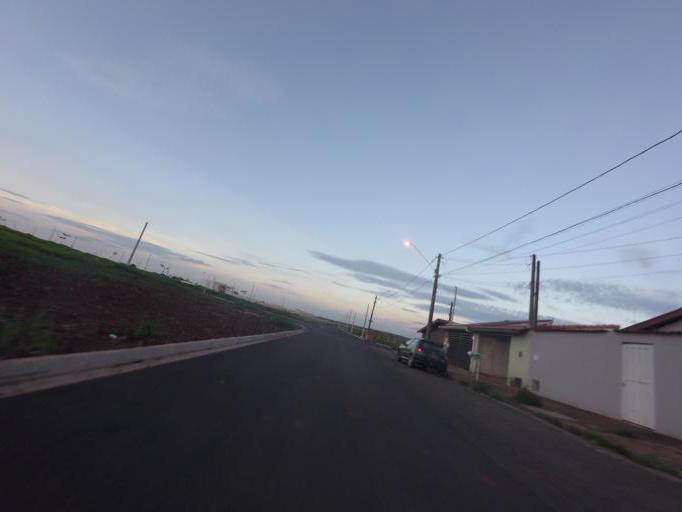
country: BR
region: Sao Paulo
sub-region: Piracicaba
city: Piracicaba
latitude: -22.7665
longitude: -47.5858
